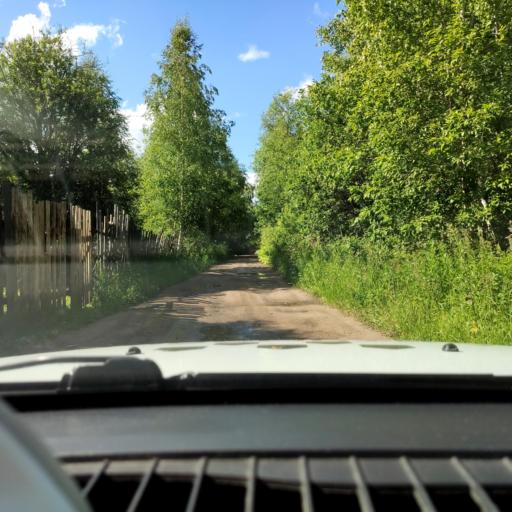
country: RU
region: Perm
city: Overyata
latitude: 58.1038
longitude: 55.8682
